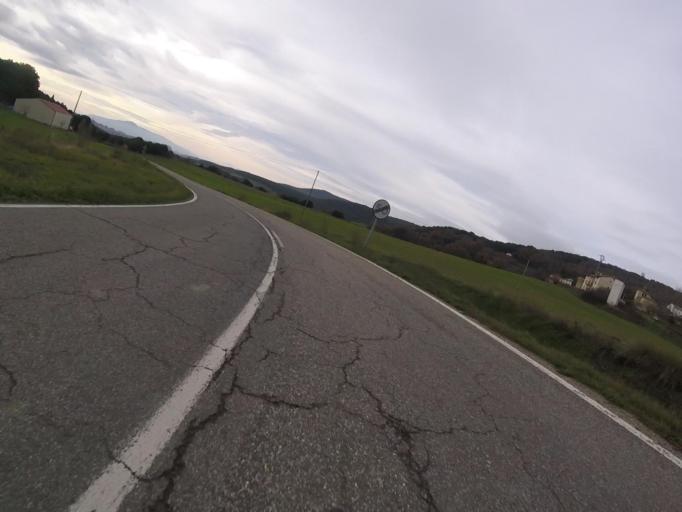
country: ES
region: Navarre
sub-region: Provincia de Navarra
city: Lezaun
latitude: 42.7463
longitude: -2.0202
